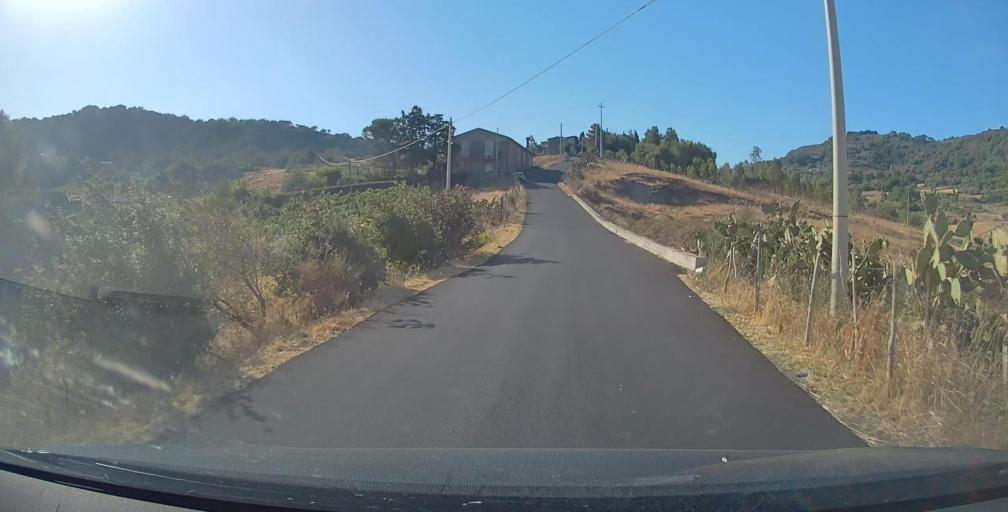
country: IT
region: Sicily
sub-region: Messina
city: San Piero Patti
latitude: 38.0605
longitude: 14.9917
